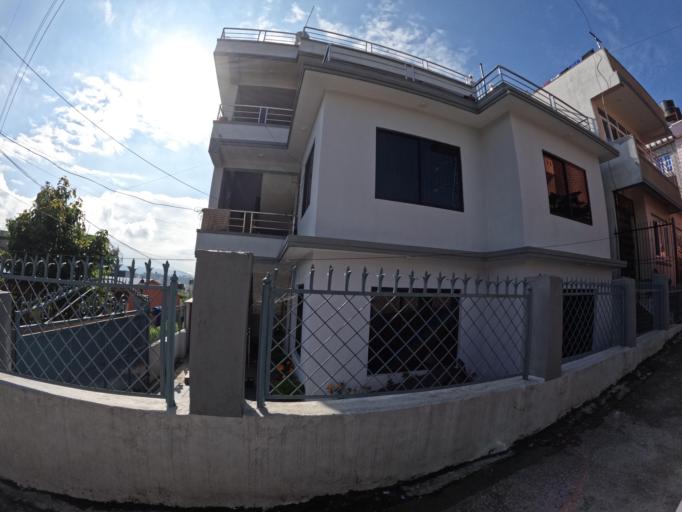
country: NP
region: Central Region
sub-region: Bagmati Zone
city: Kathmandu
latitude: 27.7613
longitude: 85.3309
